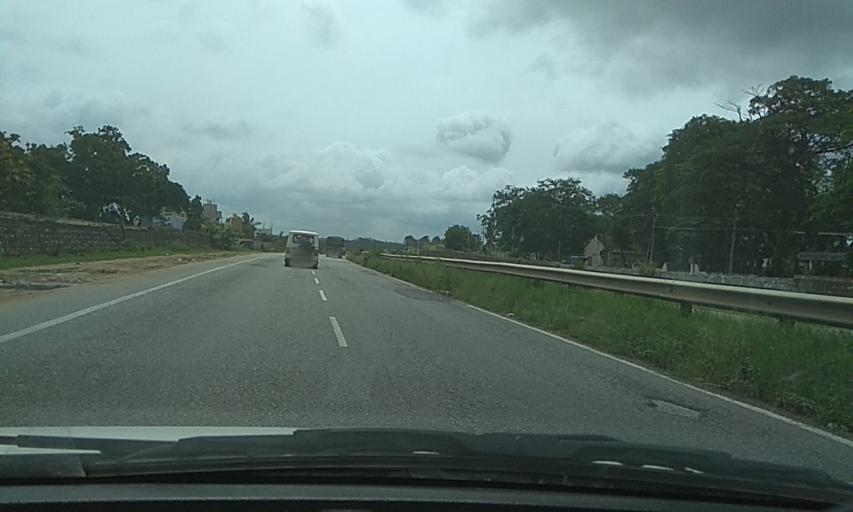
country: IN
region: Karnataka
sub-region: Davanagere
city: Mayakonda
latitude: 14.3932
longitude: 76.0448
